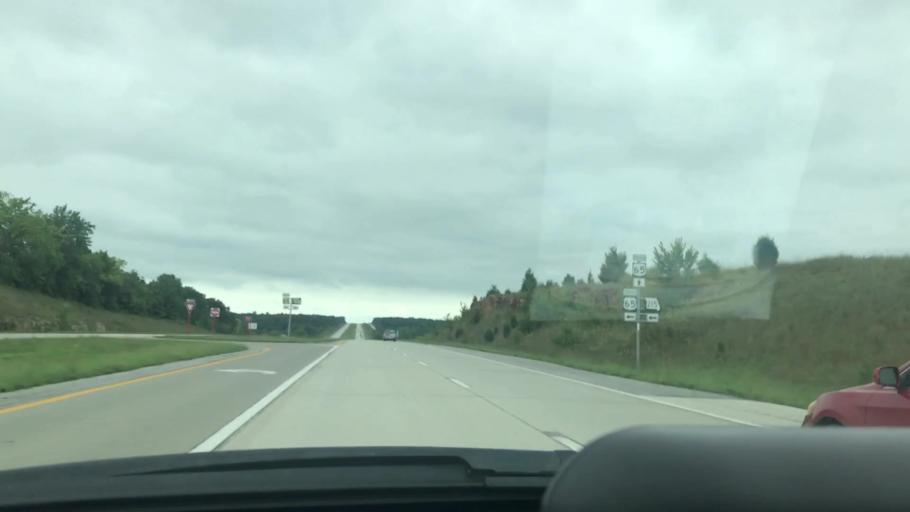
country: US
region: Missouri
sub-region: Greene County
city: Fair Grove
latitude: 37.4607
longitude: -93.1397
